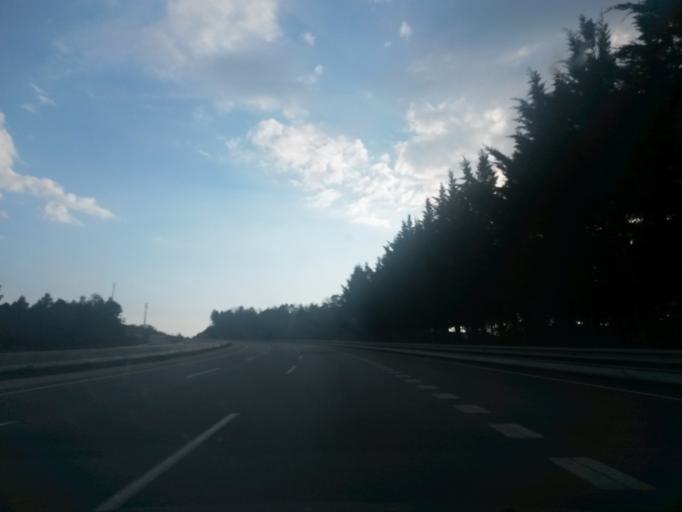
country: ES
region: Catalonia
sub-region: Provincia de Barcelona
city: Sant Julia de Vilatorta
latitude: 41.8951
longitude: 2.3661
